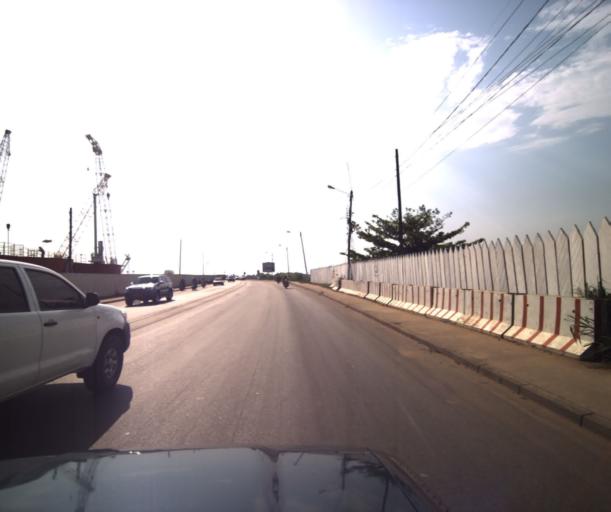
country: CM
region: Littoral
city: Bonaberi
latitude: 4.0725
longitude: 9.6975
